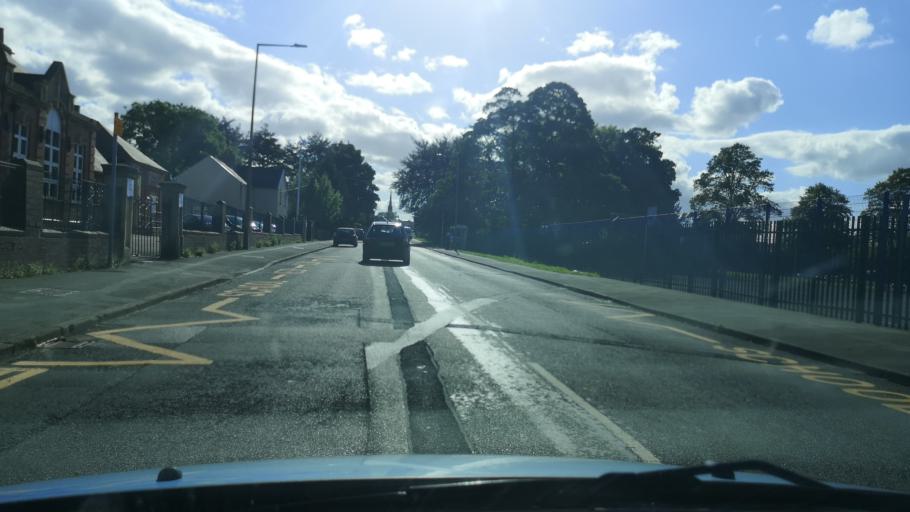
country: GB
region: England
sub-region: Doncaster
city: Carcroft
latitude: 53.5674
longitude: -1.1891
